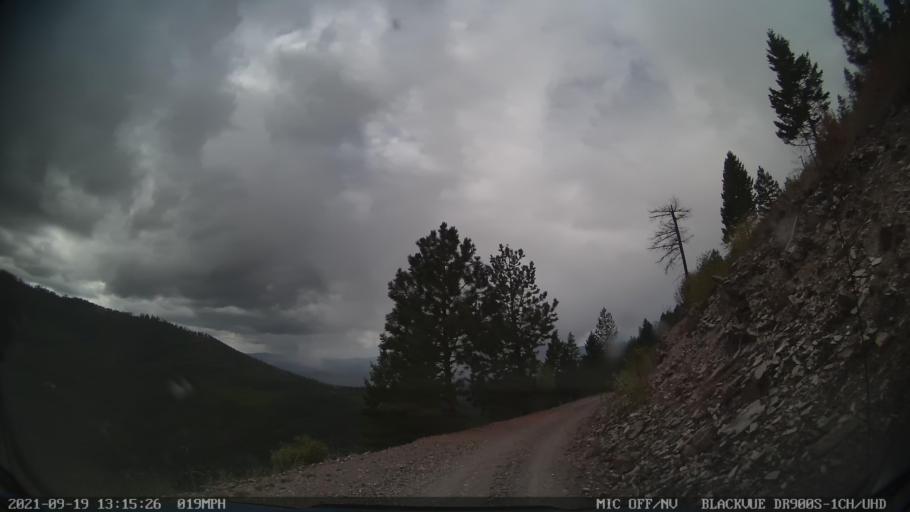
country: US
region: Montana
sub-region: Missoula County
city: Seeley Lake
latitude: 47.1793
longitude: -113.3698
